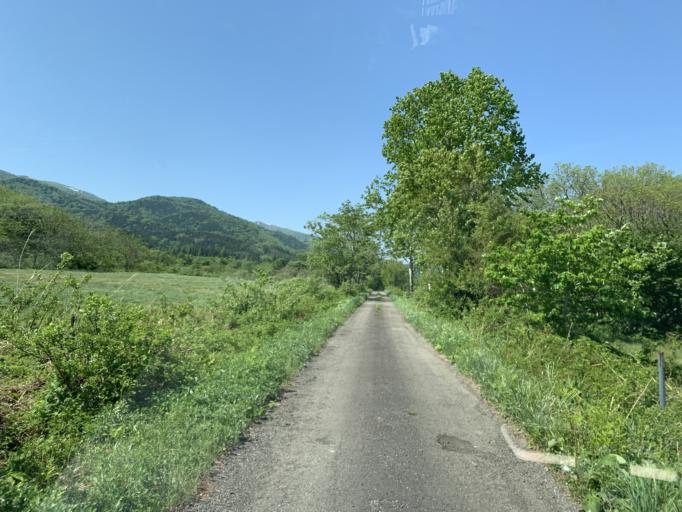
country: JP
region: Iwate
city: Shizukuishi
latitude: 39.5524
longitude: 140.8211
